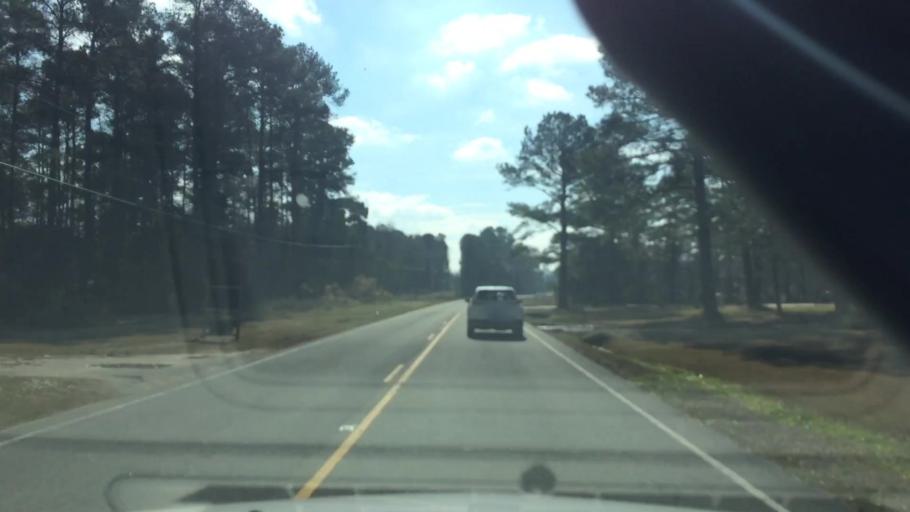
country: US
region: North Carolina
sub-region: Duplin County
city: Beulaville
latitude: 34.8709
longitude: -77.7917
